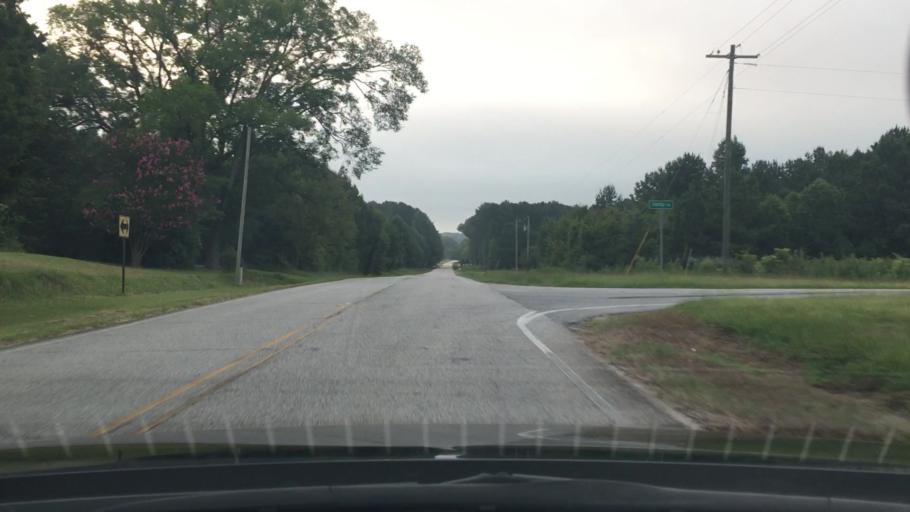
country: US
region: Georgia
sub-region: Coweta County
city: Senoia
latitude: 33.2865
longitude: -84.4388
